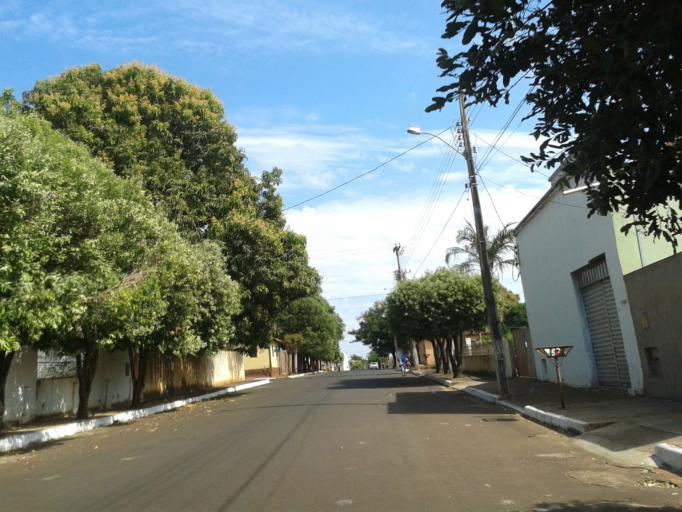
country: BR
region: Minas Gerais
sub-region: Santa Vitoria
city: Santa Vitoria
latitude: -18.8376
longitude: -50.1258
